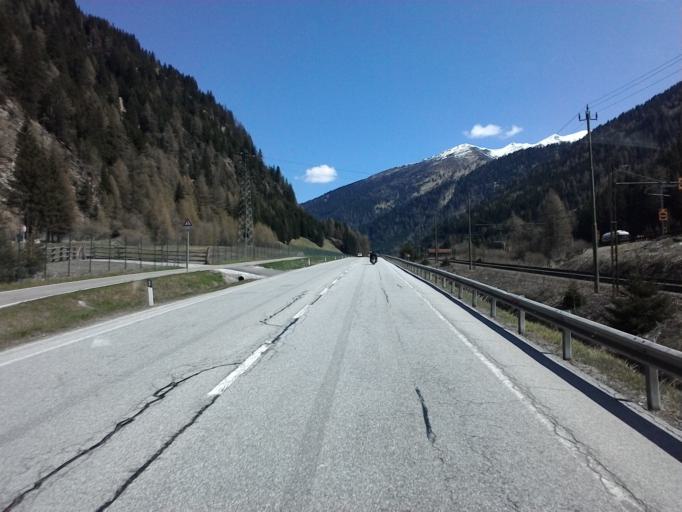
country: AT
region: Tyrol
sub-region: Politischer Bezirk Innsbruck Land
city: Gries am Brenner
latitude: 46.9908
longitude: 11.4968
